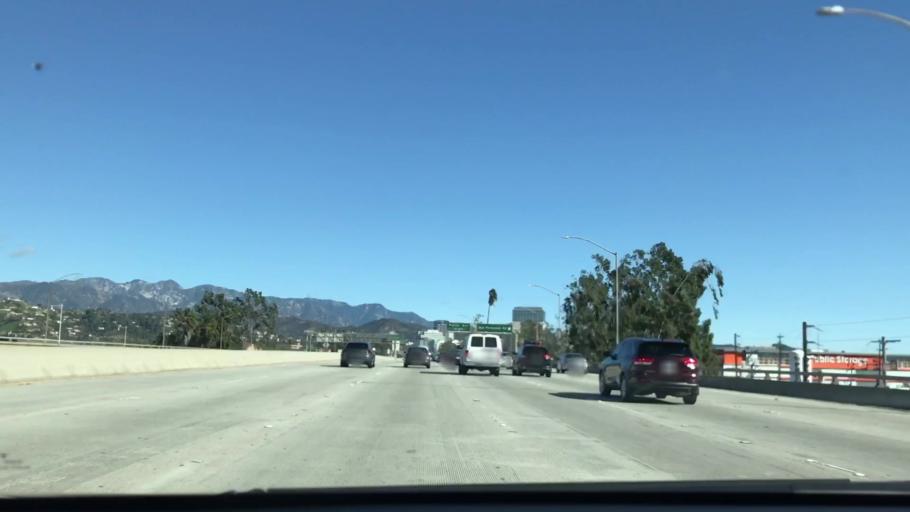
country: US
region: California
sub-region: Los Angeles County
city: North Glendale
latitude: 34.1527
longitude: -118.2777
